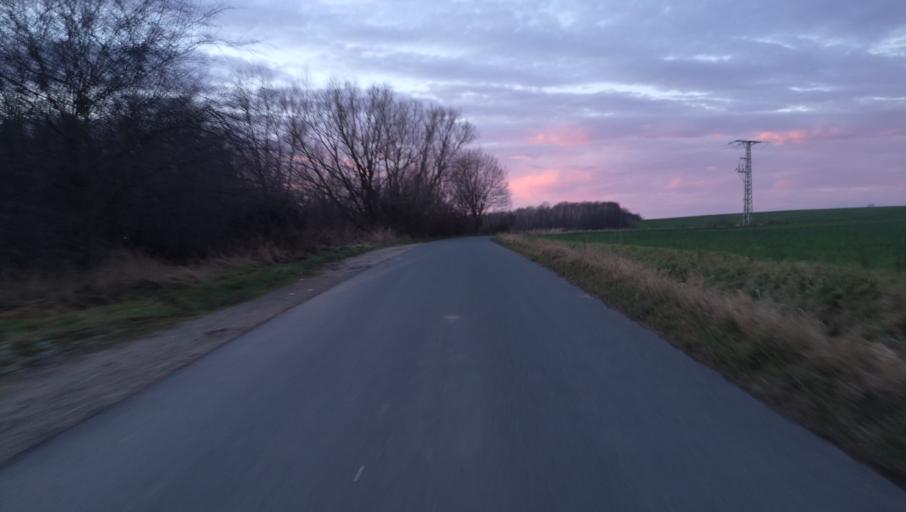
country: DE
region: Thuringia
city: Ronneburg
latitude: 50.8645
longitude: 12.1647
